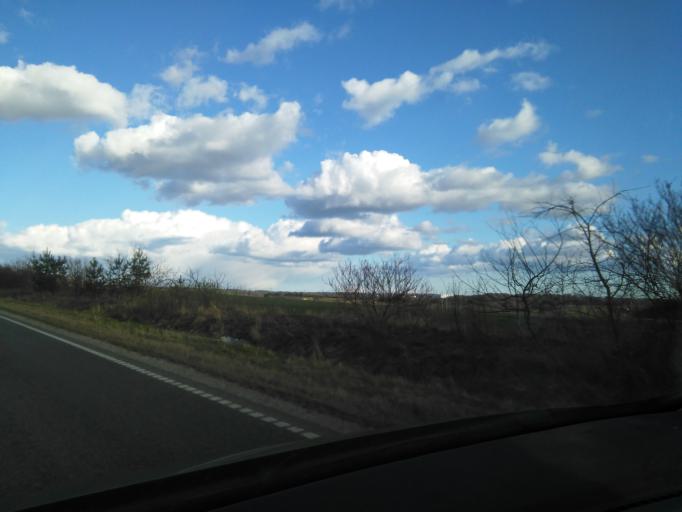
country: DK
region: Central Jutland
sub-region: Arhus Kommune
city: Framlev
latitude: 56.1853
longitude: 10.0120
